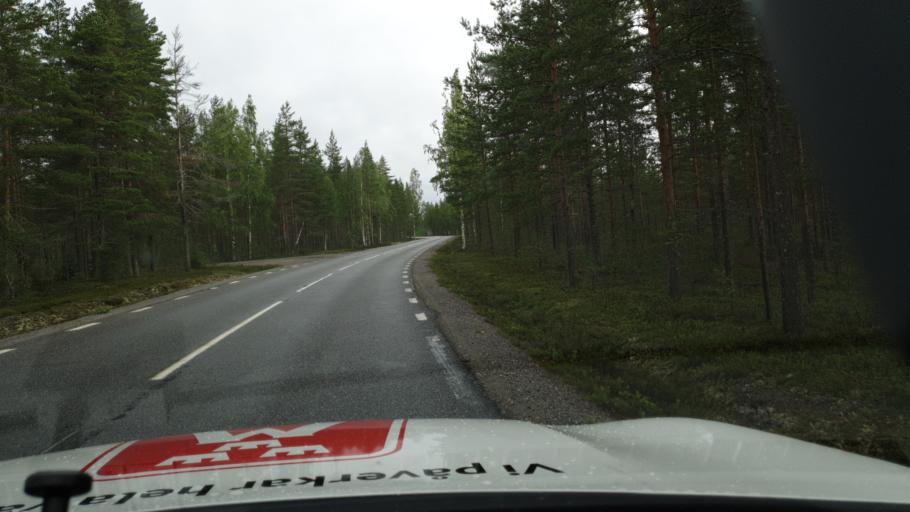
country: SE
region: Vaesterbotten
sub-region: Umea Kommun
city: Saevar
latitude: 63.9752
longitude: 20.5053
